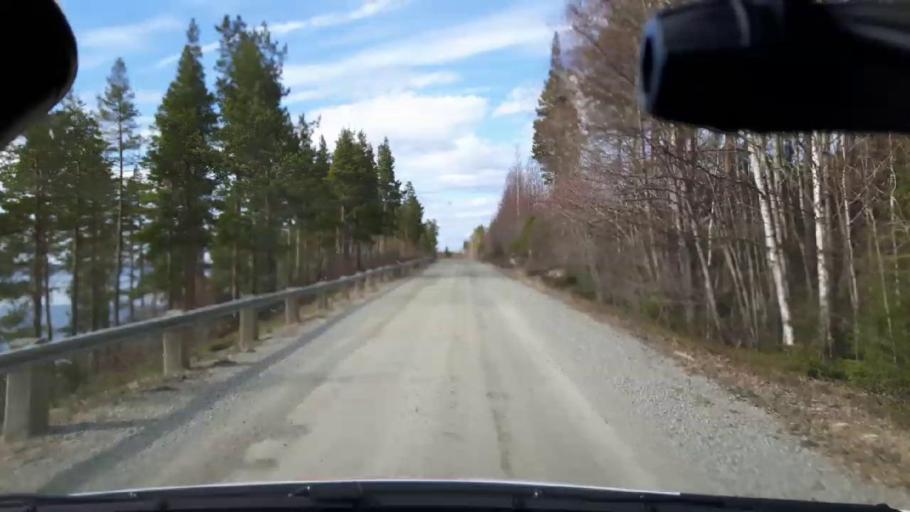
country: SE
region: Jaemtland
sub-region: Bergs Kommun
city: Hoverberg
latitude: 62.7302
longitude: 14.6655
